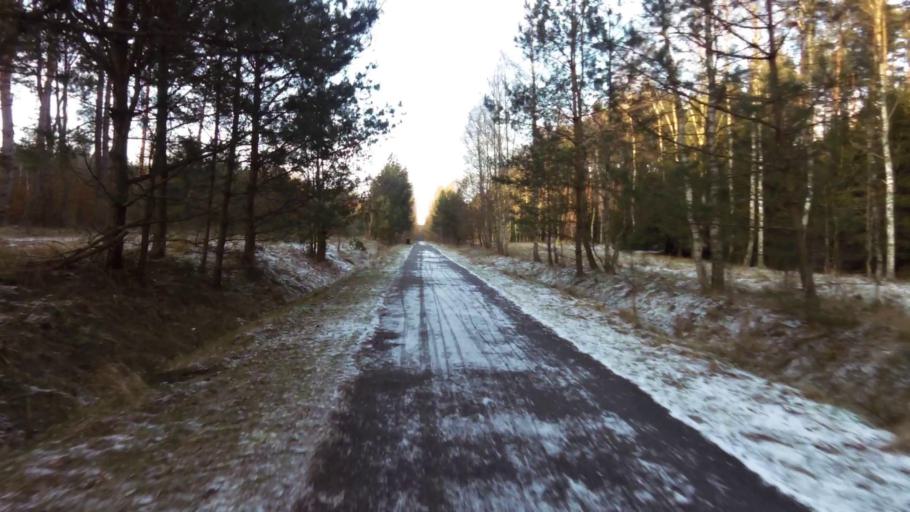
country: PL
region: West Pomeranian Voivodeship
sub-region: Powiat drawski
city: Zlocieniec
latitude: 53.5731
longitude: 16.0381
